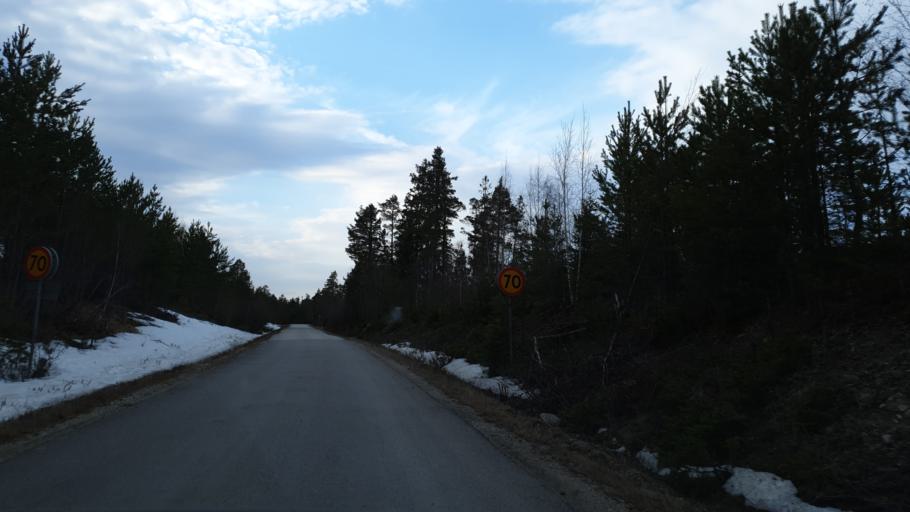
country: SE
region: Vaesternorrland
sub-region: Sundsvalls Kommun
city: Njurundabommen
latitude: 62.0233
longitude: 17.4067
